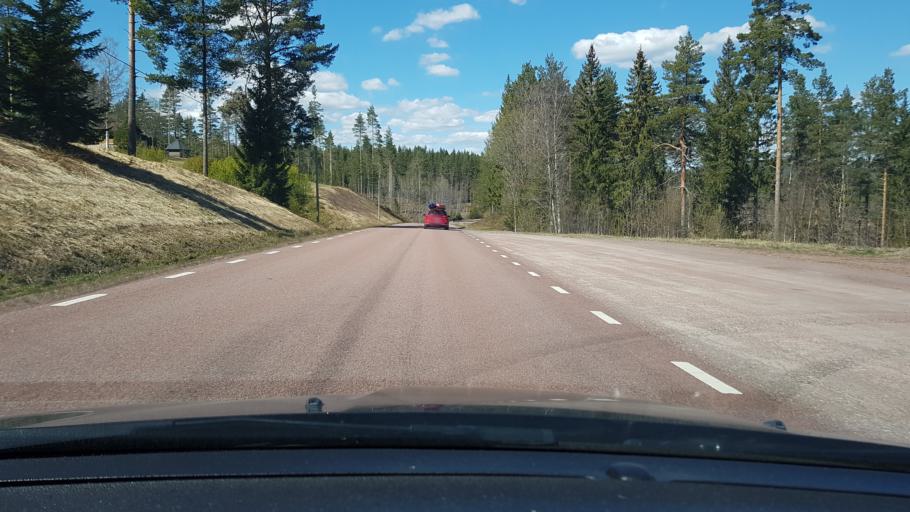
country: SE
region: Dalarna
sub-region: Alvdalens Kommun
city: AElvdalen
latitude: 61.1143
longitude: 14.1067
